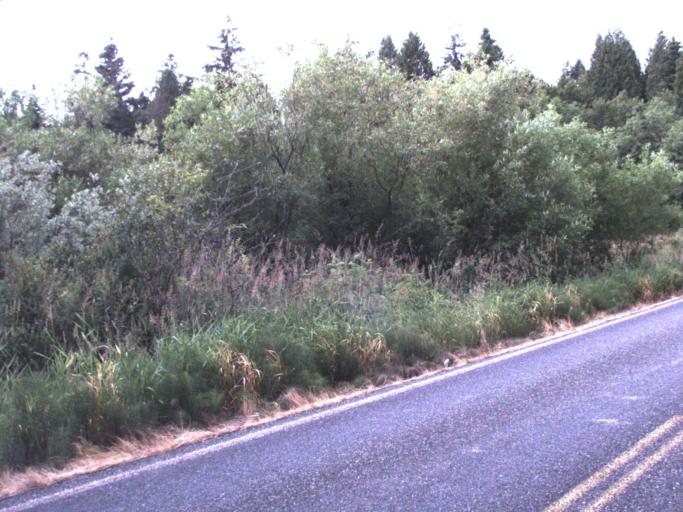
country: US
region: Washington
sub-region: Whatcom County
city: Birch Bay
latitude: 48.9281
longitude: -122.7263
